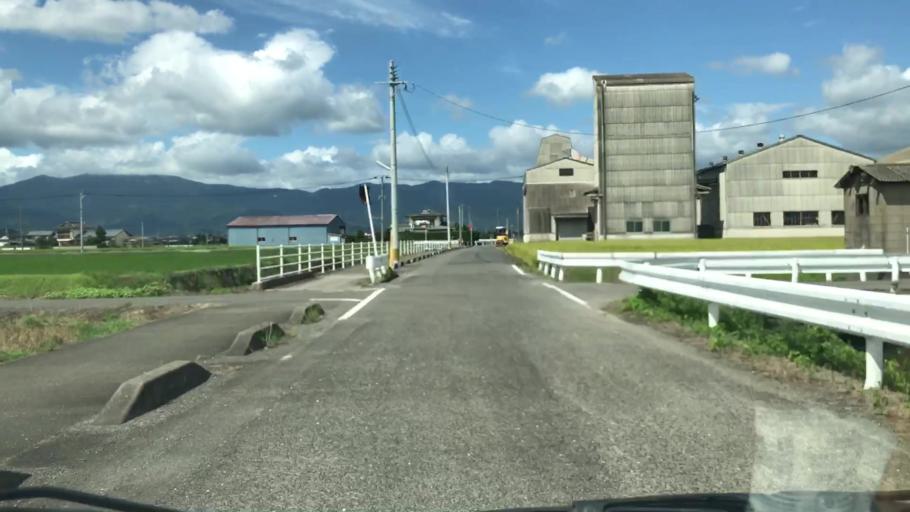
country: JP
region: Saga Prefecture
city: Saga-shi
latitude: 33.2315
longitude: 130.2122
